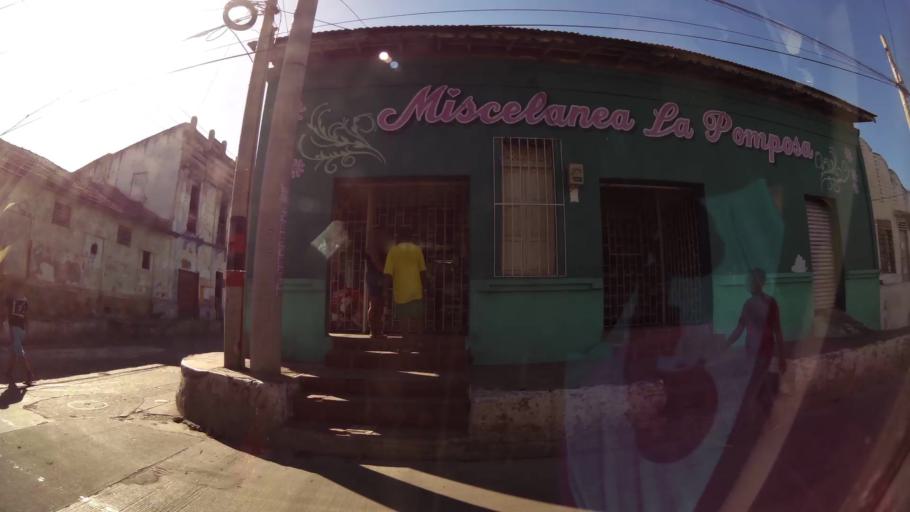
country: CO
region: Atlantico
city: Barranquilla
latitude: 10.9728
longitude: -74.7816
